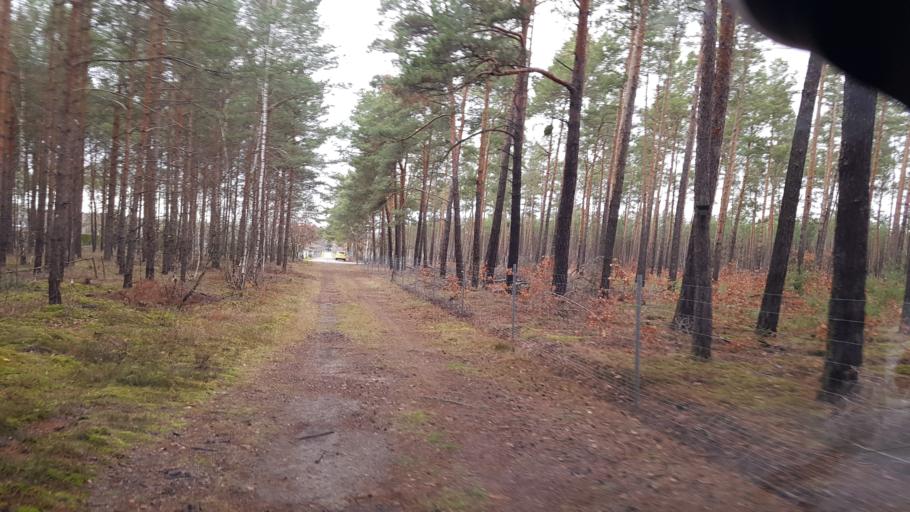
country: DE
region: Brandenburg
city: Altdobern
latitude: 51.6793
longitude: 14.0238
